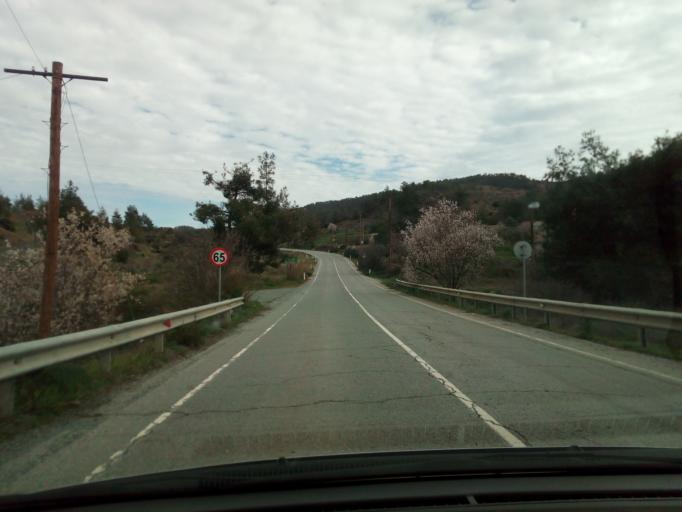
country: CY
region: Lefkosia
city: Klirou
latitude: 34.9839
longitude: 33.1588
